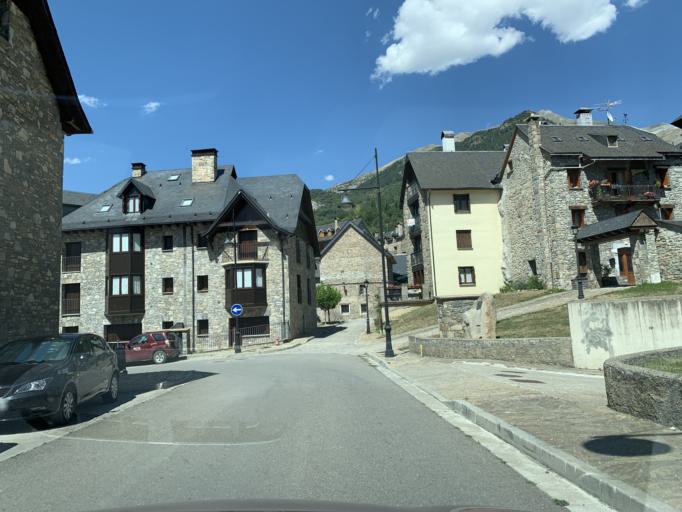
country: ES
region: Aragon
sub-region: Provincia de Huesca
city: Hoz de Jaca
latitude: 42.7184
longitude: -0.2997
